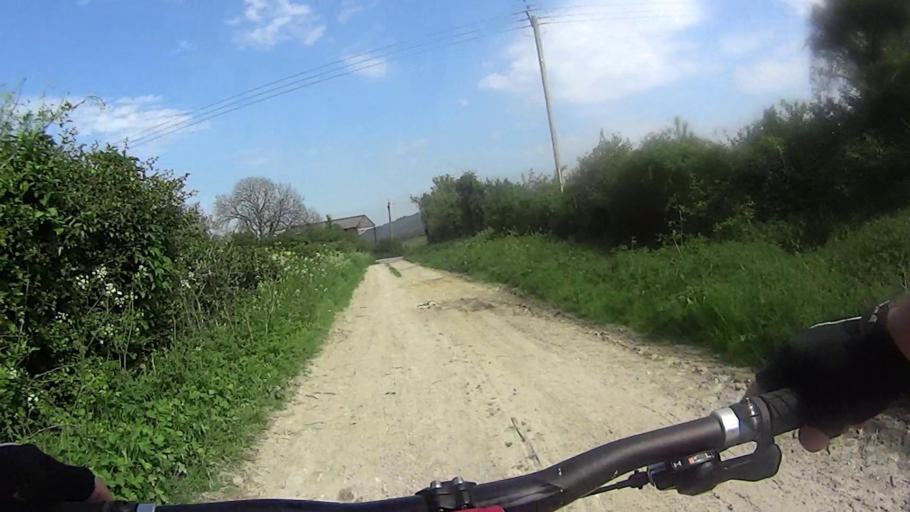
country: GB
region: England
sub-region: Hampshire
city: Petersfield
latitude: 50.9664
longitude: -0.9030
